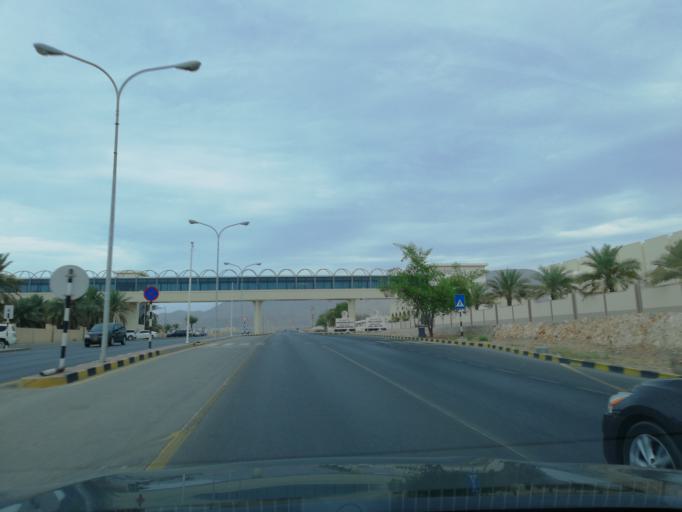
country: OM
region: Muhafazat Masqat
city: Bawshar
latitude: 23.5742
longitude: 58.3862
